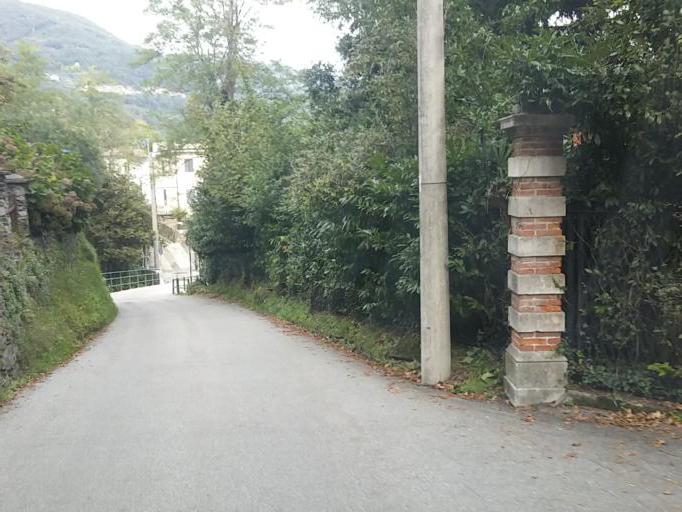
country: IT
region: Piedmont
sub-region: Provincia Verbano-Cusio-Ossola
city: Gonte
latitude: 45.9984
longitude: 8.6555
